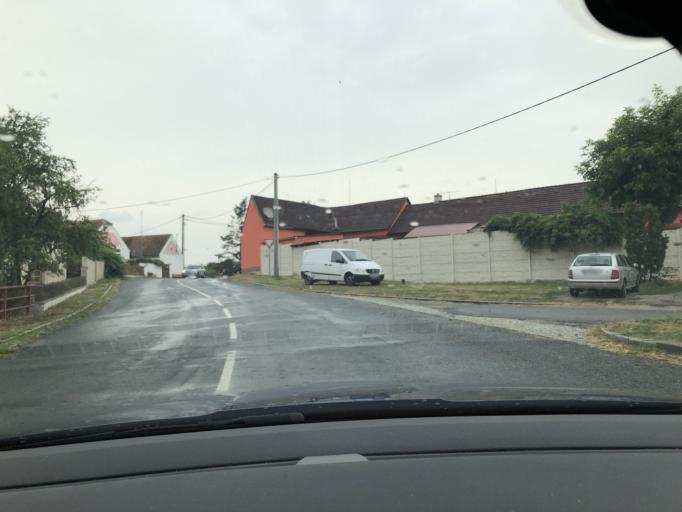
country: CZ
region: South Moravian
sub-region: Okres Znojmo
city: Jevisovice
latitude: 49.0272
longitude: 15.9759
